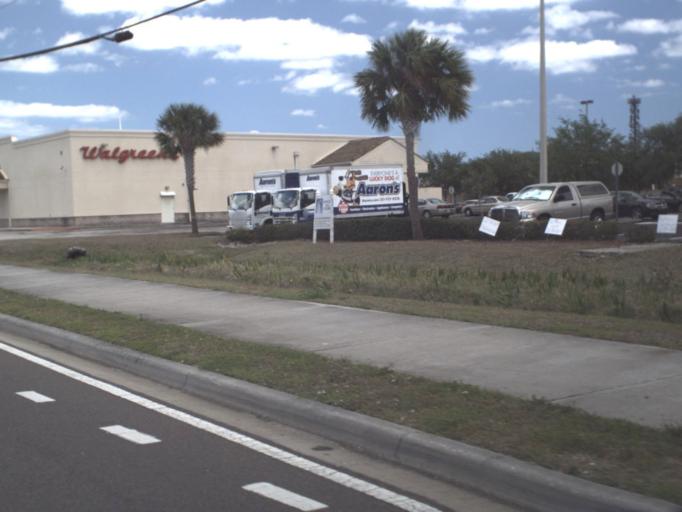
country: US
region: Florida
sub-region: Brevard County
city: Palm Bay
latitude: 28.0177
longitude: -80.6221
